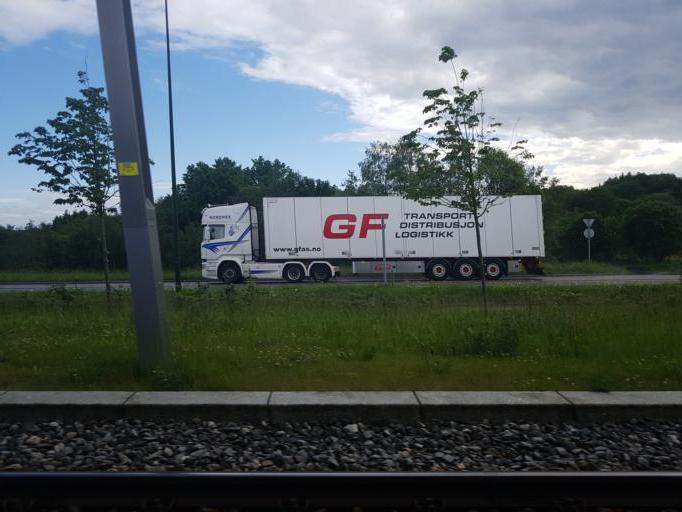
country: NO
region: Hordaland
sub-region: Bergen
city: Ytrebygda
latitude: 60.2923
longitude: 5.2414
